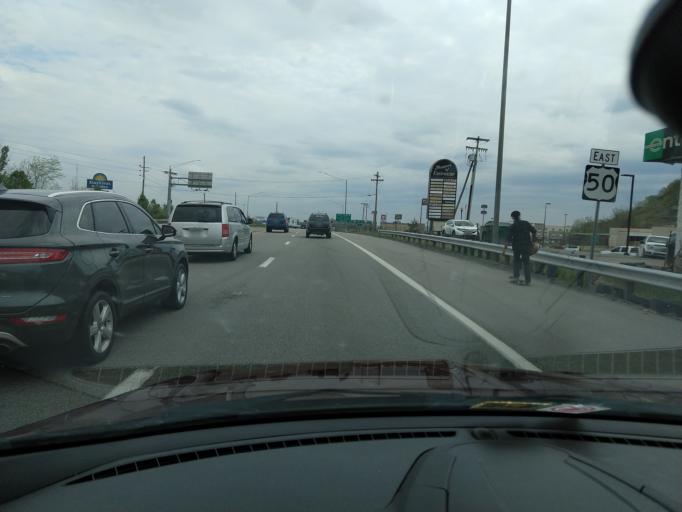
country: US
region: West Virginia
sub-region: Harrison County
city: Despard
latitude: 39.2796
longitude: -80.2817
